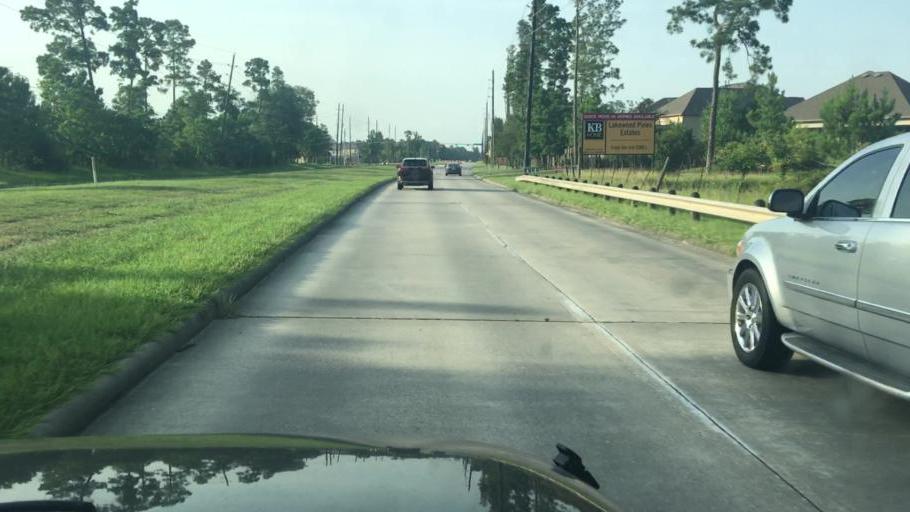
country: US
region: Texas
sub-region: Harris County
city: Atascocita
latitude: 29.9422
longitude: -95.1755
